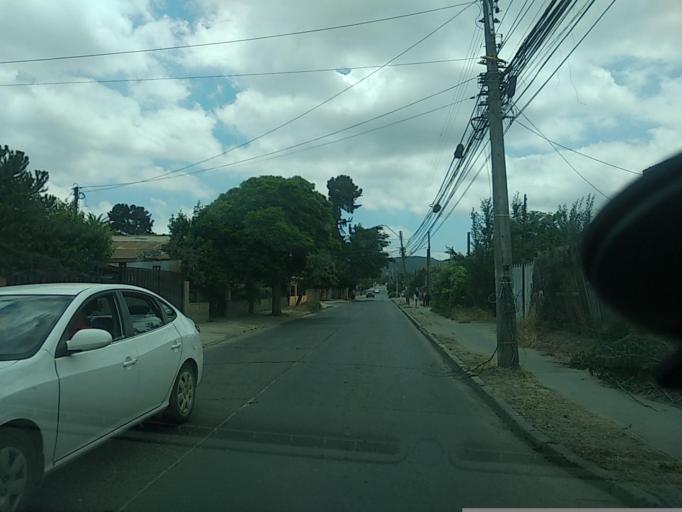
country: CL
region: Valparaiso
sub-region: Provincia de Marga Marga
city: Villa Alemana
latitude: -33.0425
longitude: -71.4054
